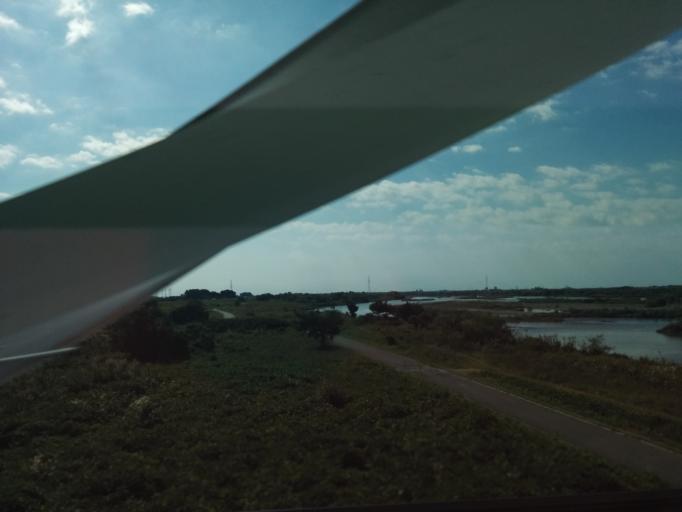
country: JP
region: Shizuoka
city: Iwata
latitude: 34.7046
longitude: 137.8051
